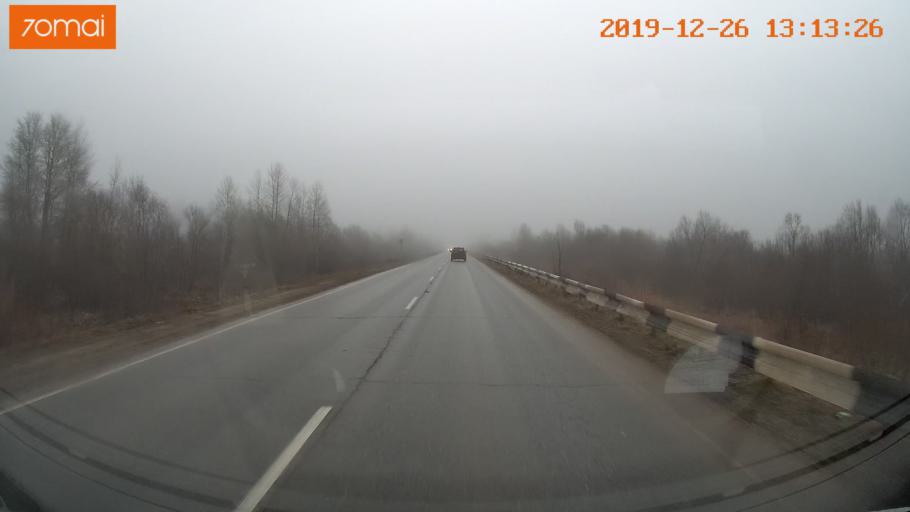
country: RU
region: Vologda
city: Cherepovets
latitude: 59.0180
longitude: 38.0525
